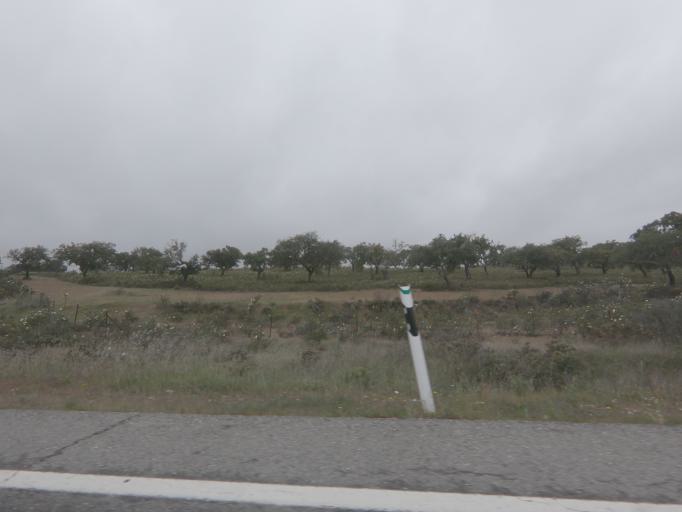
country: ES
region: Extremadura
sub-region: Provincia de Caceres
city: Malpartida de Caceres
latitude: 39.3047
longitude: -6.5161
